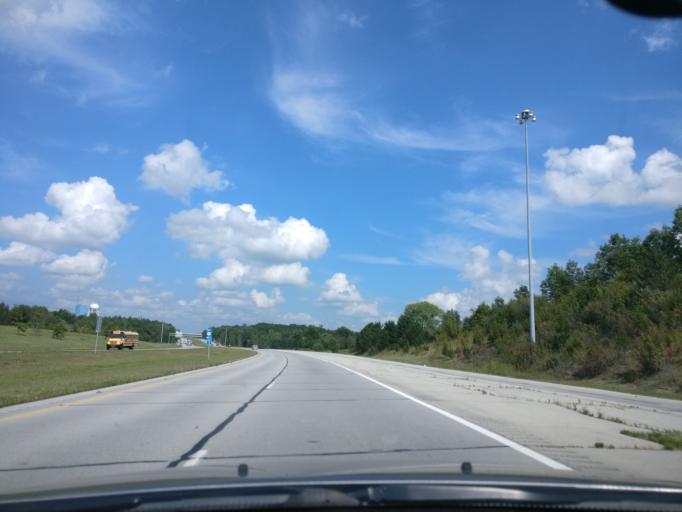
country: US
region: Ohio
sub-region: Greene County
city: Xenia
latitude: 39.6651
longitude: -83.9131
